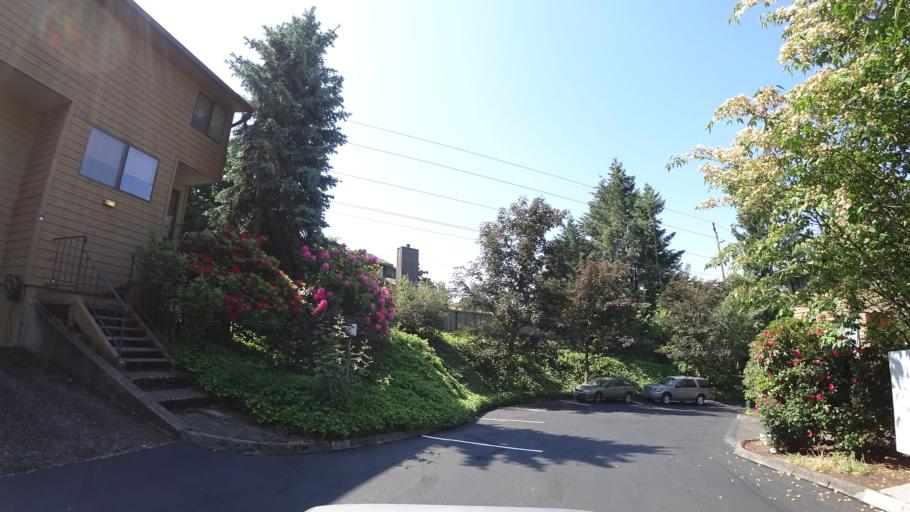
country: US
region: Oregon
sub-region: Washington County
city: Durham
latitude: 45.4261
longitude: -122.7215
